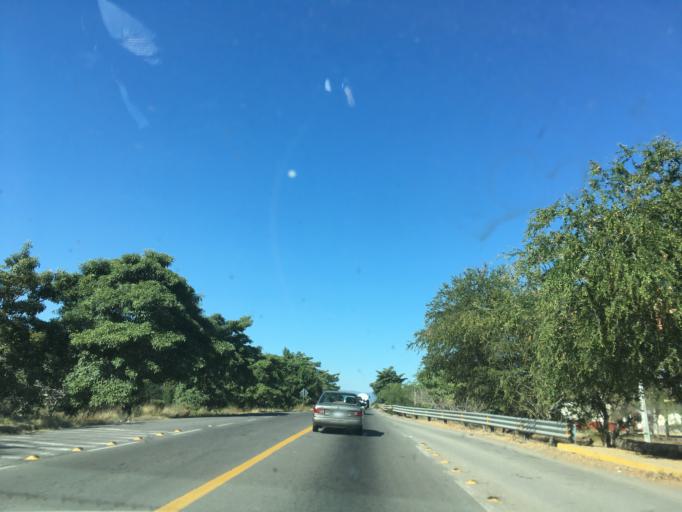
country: MX
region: Michoacan
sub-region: Gabriel Zamora
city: Lombardia
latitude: 19.0882
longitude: -102.0587
